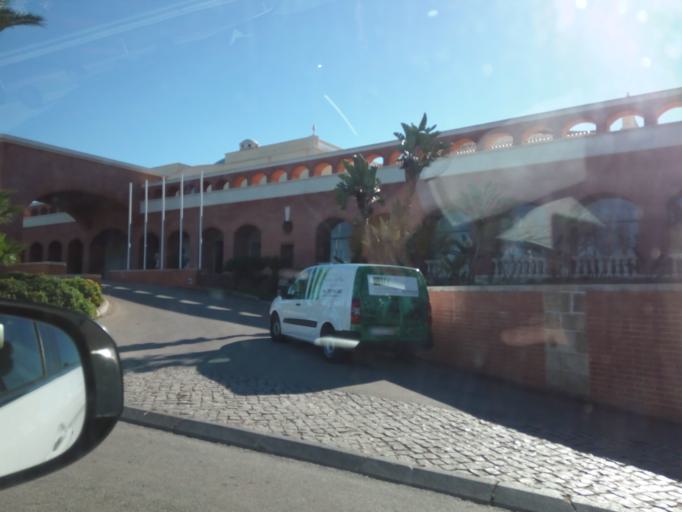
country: PT
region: Faro
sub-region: Loule
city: Vilamoura
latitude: 37.0791
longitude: -8.1269
